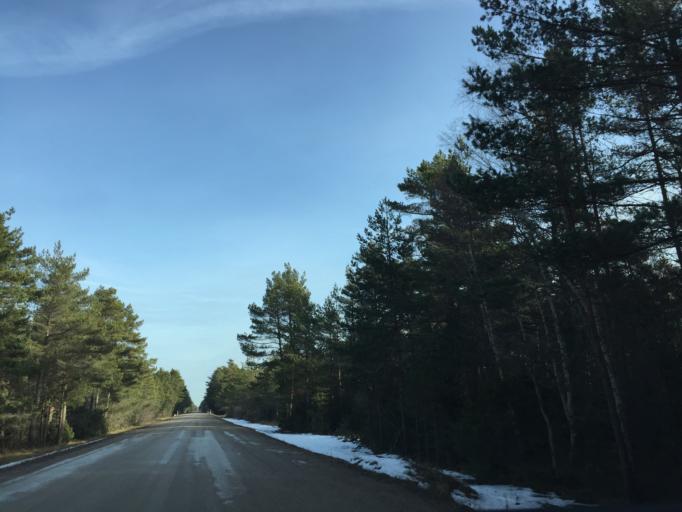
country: EE
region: Saare
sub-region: Kuressaare linn
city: Kuressaare
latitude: 58.2980
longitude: 21.9522
